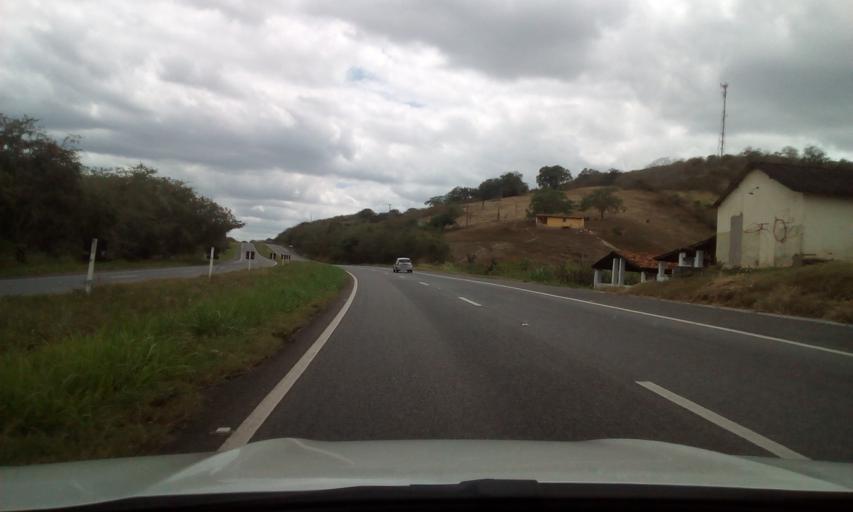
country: BR
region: Paraiba
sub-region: Fagundes
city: Fagundes
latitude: -7.2782
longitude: -35.7576
